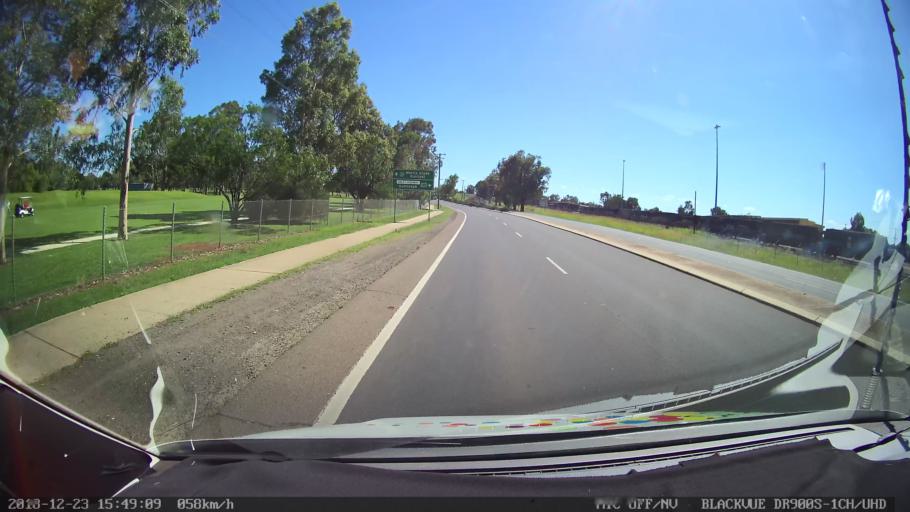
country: AU
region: New South Wales
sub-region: Tamworth Municipality
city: South Tamworth
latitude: -31.0972
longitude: 150.9086
